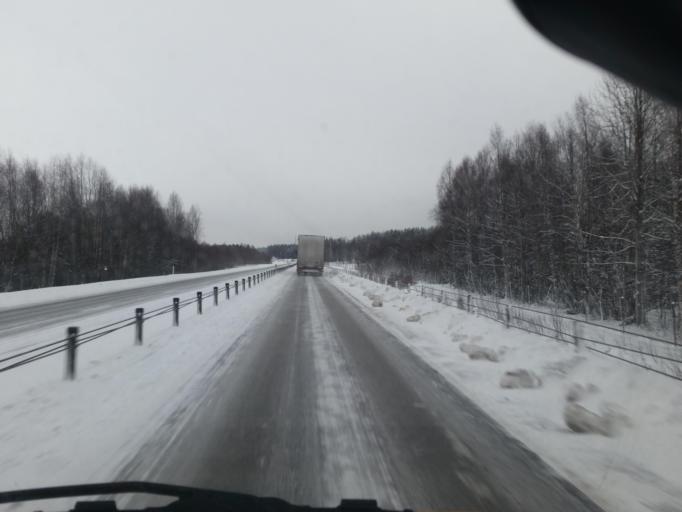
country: SE
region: Norrbotten
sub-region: Pitea Kommun
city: Pitea
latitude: 65.2618
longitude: 21.4650
